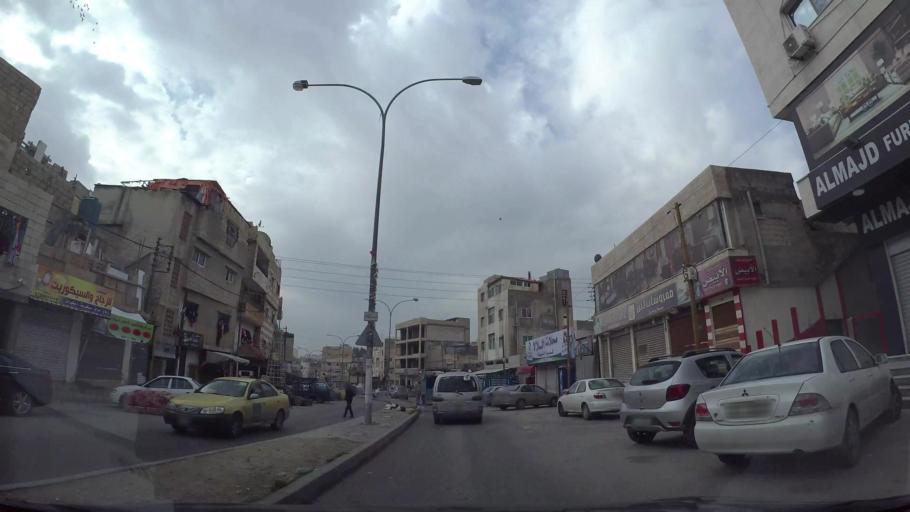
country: JO
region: Amman
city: Amman
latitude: 31.9676
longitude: 35.9264
